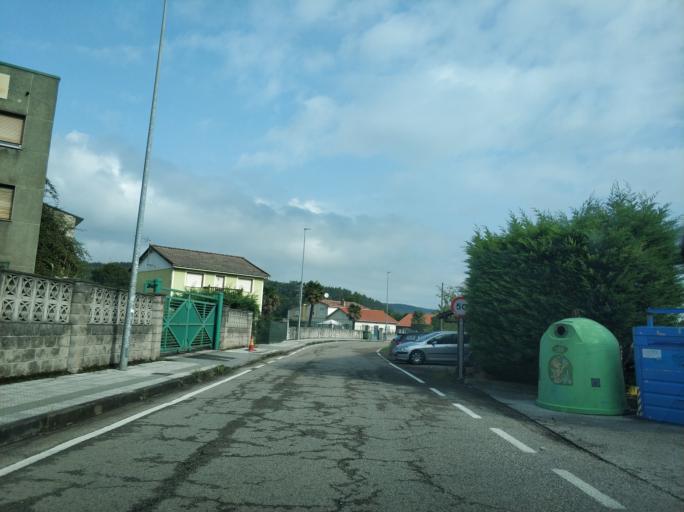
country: ES
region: Cantabria
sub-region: Provincia de Cantabria
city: Polanco
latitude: 43.3579
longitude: -3.9644
